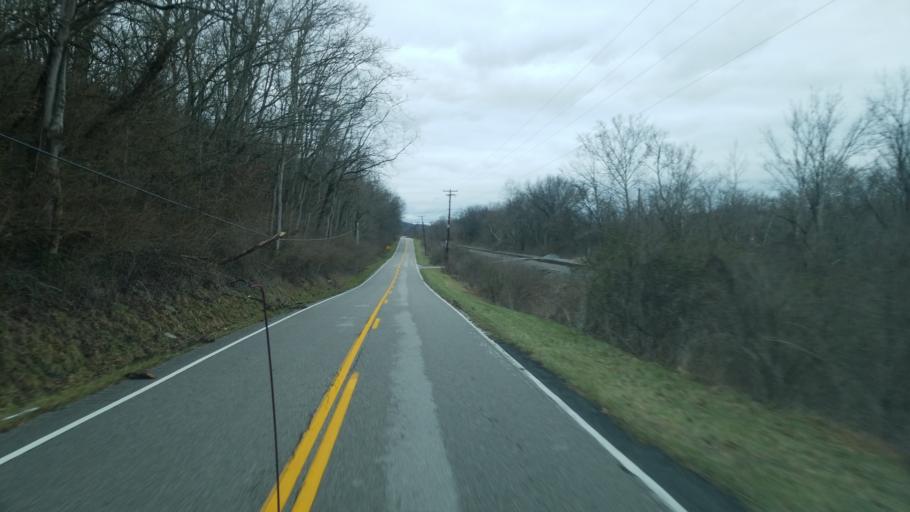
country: US
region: Ohio
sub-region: Clermont County
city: New Richmond
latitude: 38.9257
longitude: -84.2731
